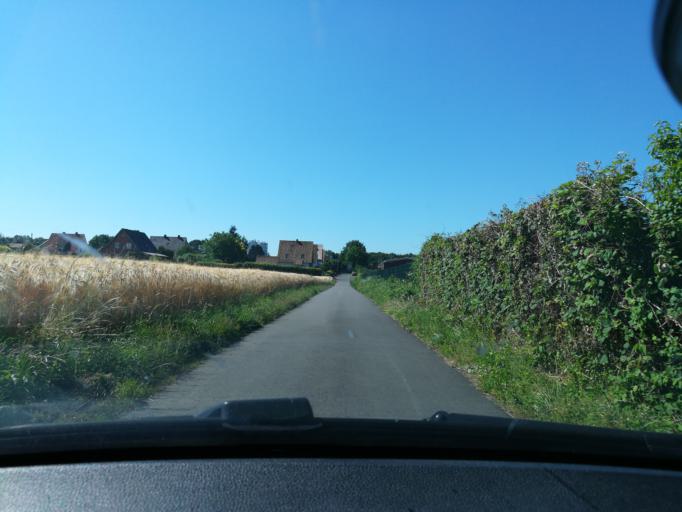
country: DE
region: North Rhine-Westphalia
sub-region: Regierungsbezirk Detmold
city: Minden
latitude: 52.3079
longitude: 8.9425
